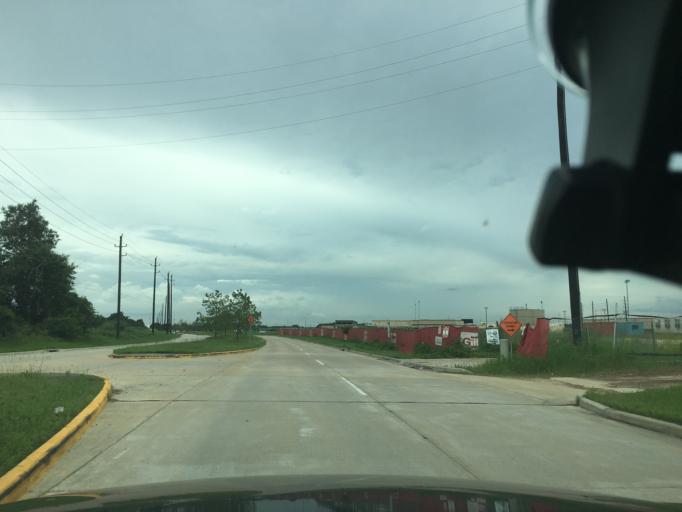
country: US
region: Texas
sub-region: Harris County
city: Tomball
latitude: 30.0641
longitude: -95.6998
